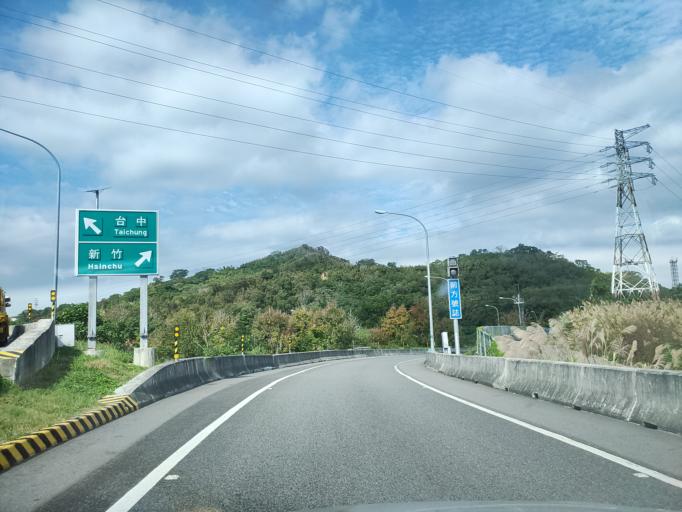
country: TW
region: Taiwan
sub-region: Miaoli
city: Miaoli
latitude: 24.5794
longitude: 120.8582
